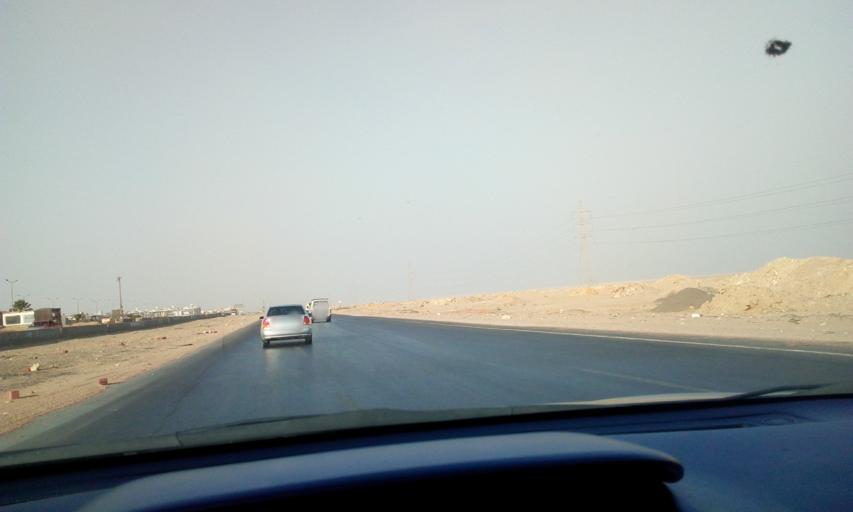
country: EG
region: Al Jizah
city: Madinat Sittah Uktubar
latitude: 29.8809
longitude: 31.0779
